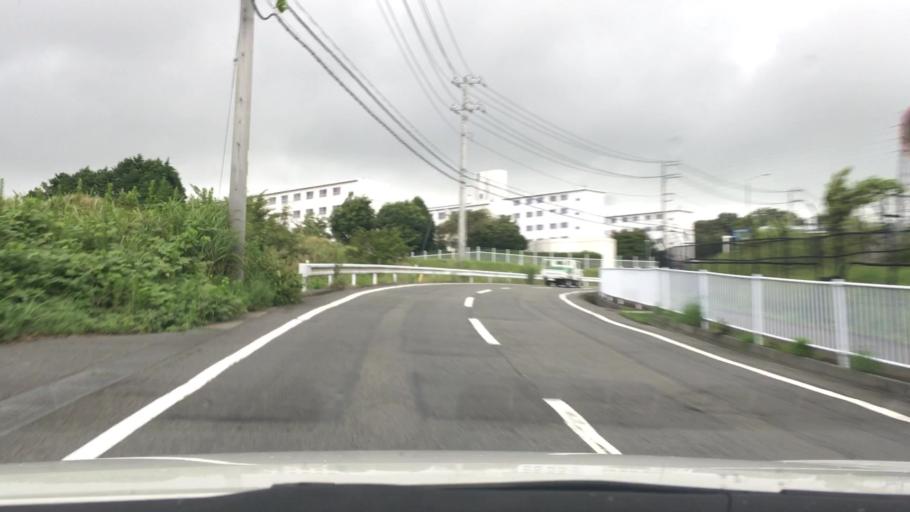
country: JP
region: Shizuoka
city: Gotemba
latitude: 35.2270
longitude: 138.8920
